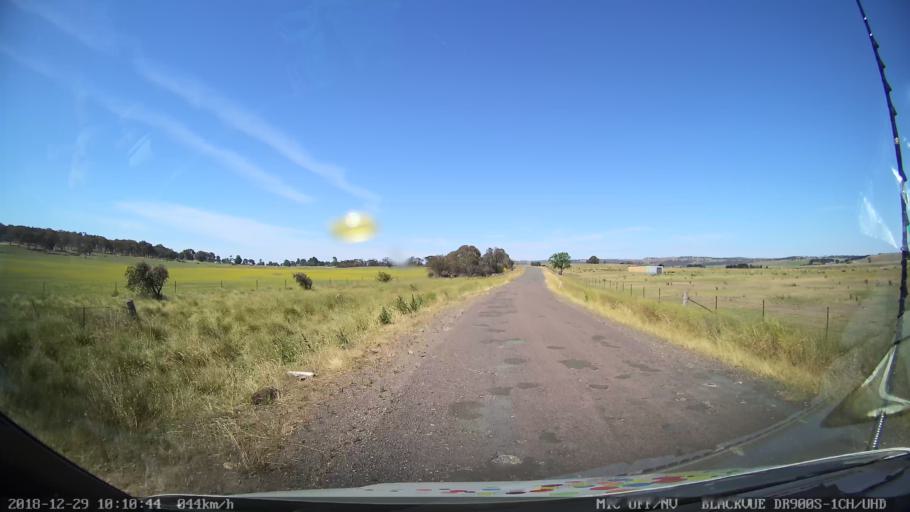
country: AU
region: New South Wales
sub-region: Yass Valley
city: Gundaroo
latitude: -34.8782
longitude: 149.4556
